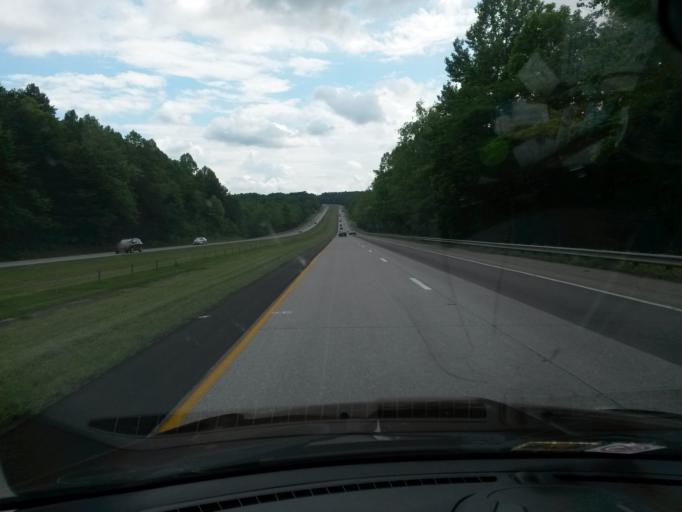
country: US
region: Virginia
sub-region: Carroll County
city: Cana
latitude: 36.5497
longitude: -80.7441
